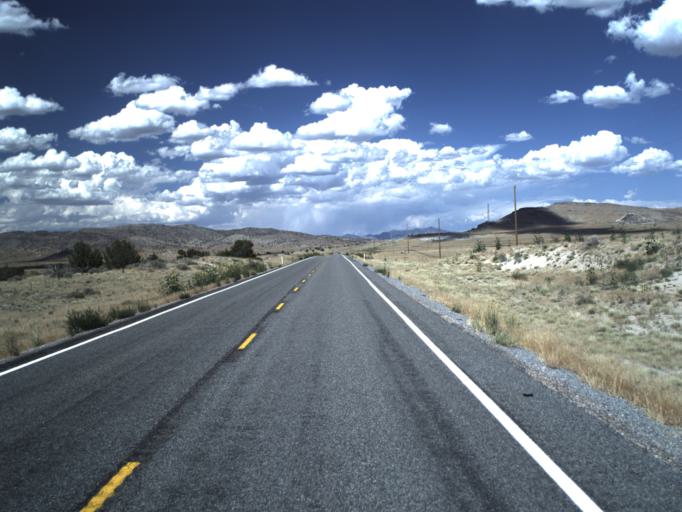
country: US
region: Utah
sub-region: Millard County
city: Delta
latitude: 39.6271
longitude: -112.3113
